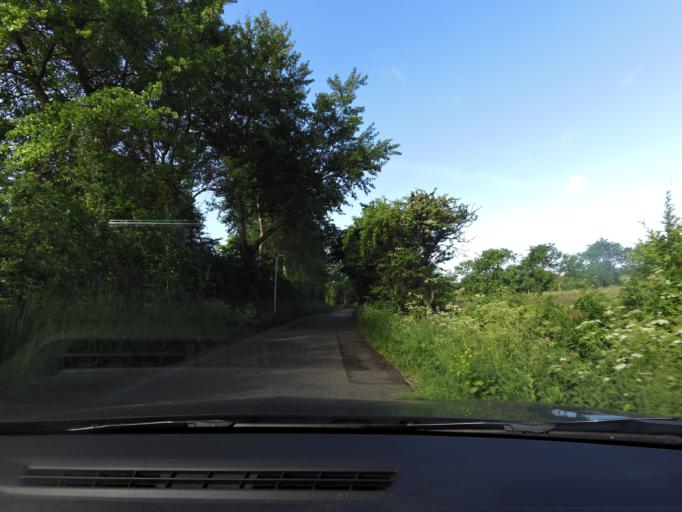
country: NL
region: Zeeland
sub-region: Schouwen-Duiveland
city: Renesse
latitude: 51.7386
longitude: 3.7824
